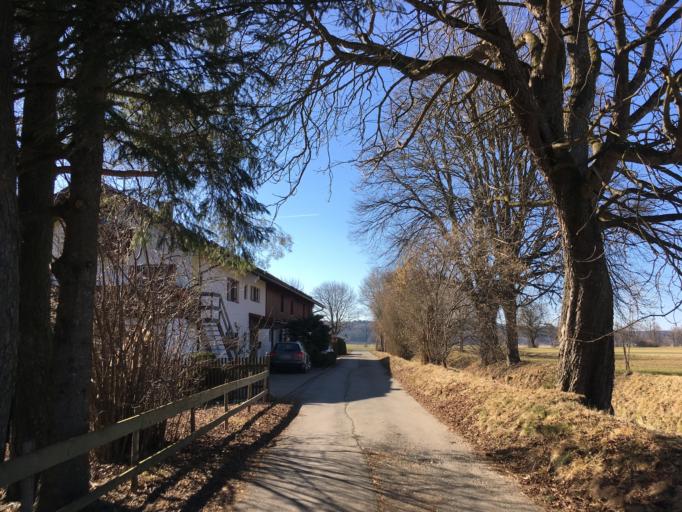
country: DE
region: Bavaria
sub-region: Upper Bavaria
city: Bad Aibling
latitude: 47.8529
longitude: 11.9833
